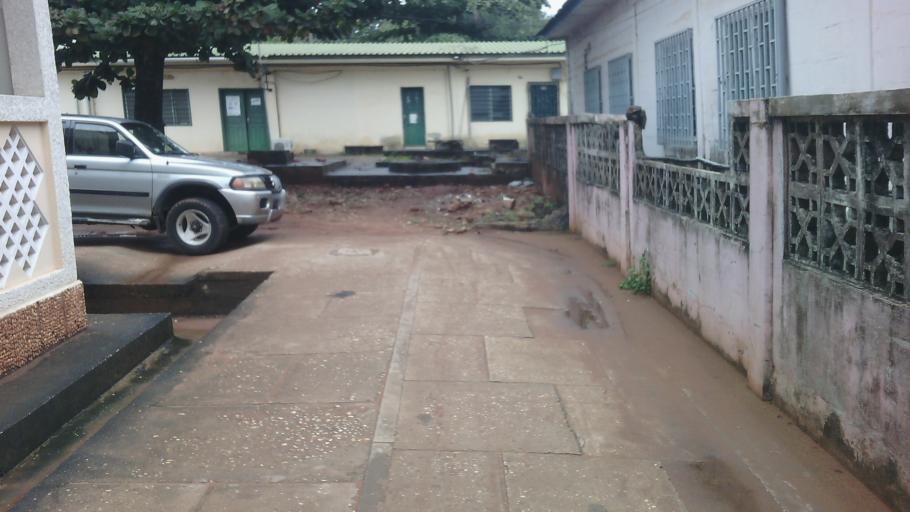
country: BJ
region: Queme
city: Porto-Novo
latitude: 6.4730
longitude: 2.6138
